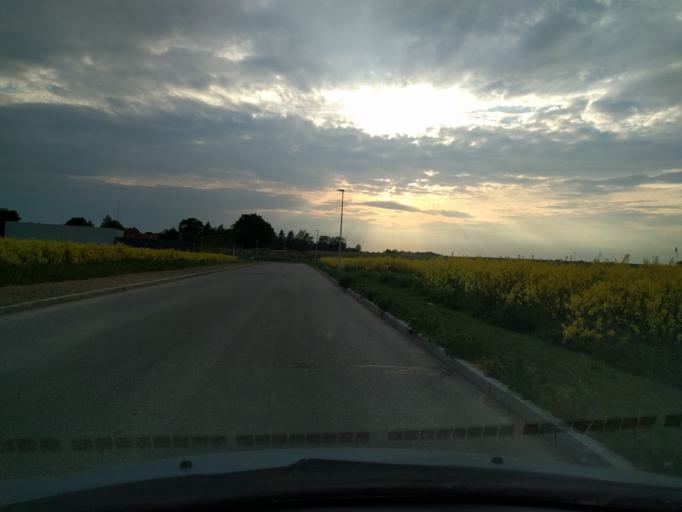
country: DK
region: Zealand
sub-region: Guldborgsund Kommune
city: Norre Alslev
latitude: 54.8992
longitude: 11.9176
